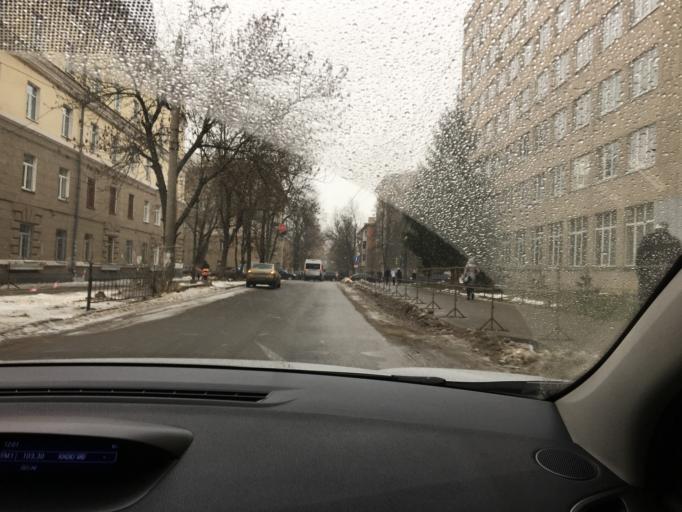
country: RU
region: Tula
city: Mendeleyevskiy
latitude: 54.1671
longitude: 37.5853
